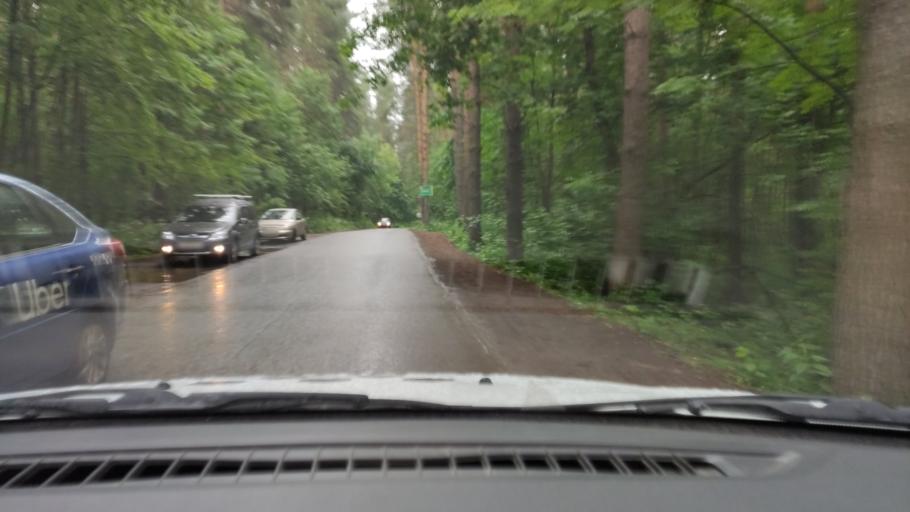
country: RU
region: Udmurtiya
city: Izhevsk
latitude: 56.8851
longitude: 53.1842
